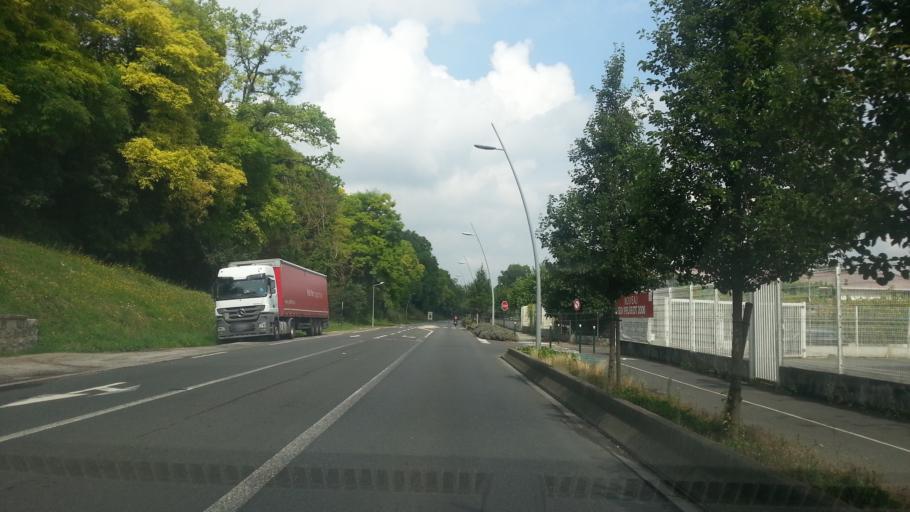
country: FR
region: Picardie
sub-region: Departement de l'Oise
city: Saint-Maximin
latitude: 49.2222
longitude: 2.4282
